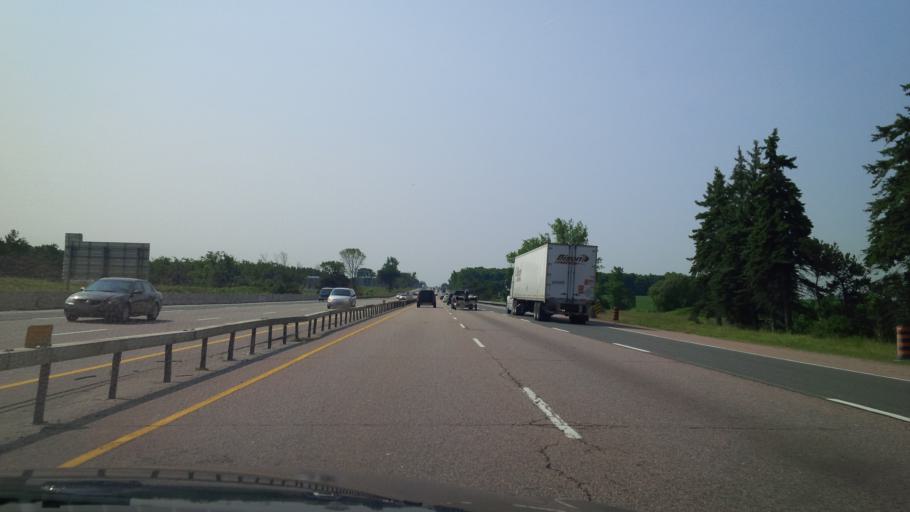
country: CA
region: Ontario
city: Innisfil
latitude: 44.2760
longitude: -79.6773
